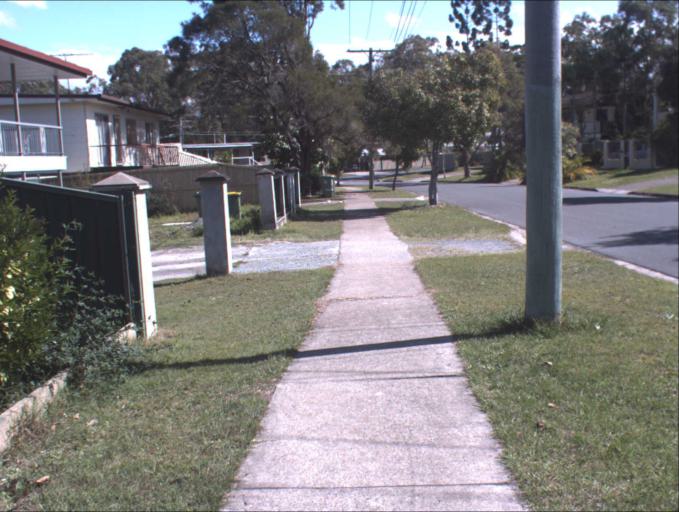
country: AU
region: Queensland
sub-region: Logan
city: Waterford West
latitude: -27.6846
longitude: 153.1075
